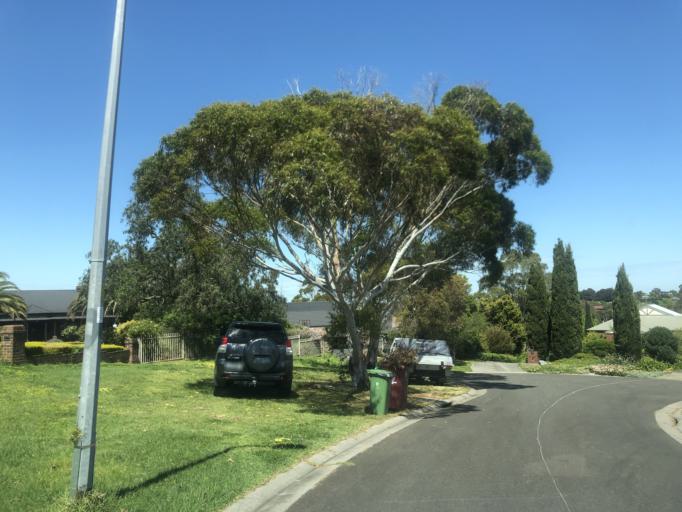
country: AU
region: Victoria
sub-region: Casey
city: Narre Warren North
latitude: -37.9847
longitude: 145.2875
